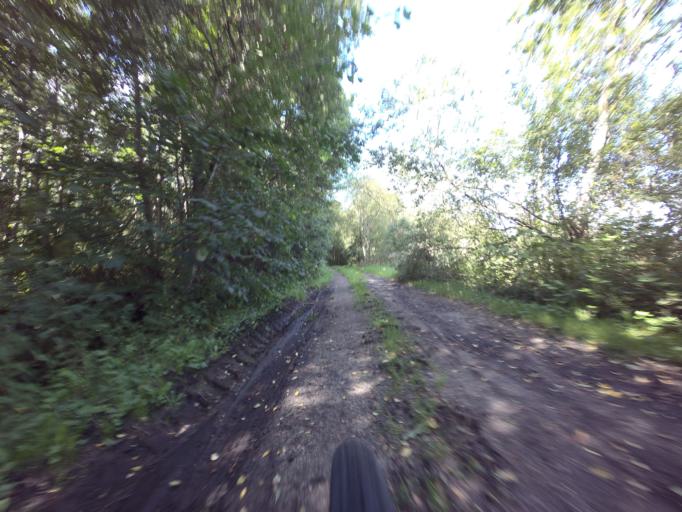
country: DK
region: Central Jutland
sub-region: Norddjurs Kommune
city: Auning
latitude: 56.4389
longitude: 10.3552
